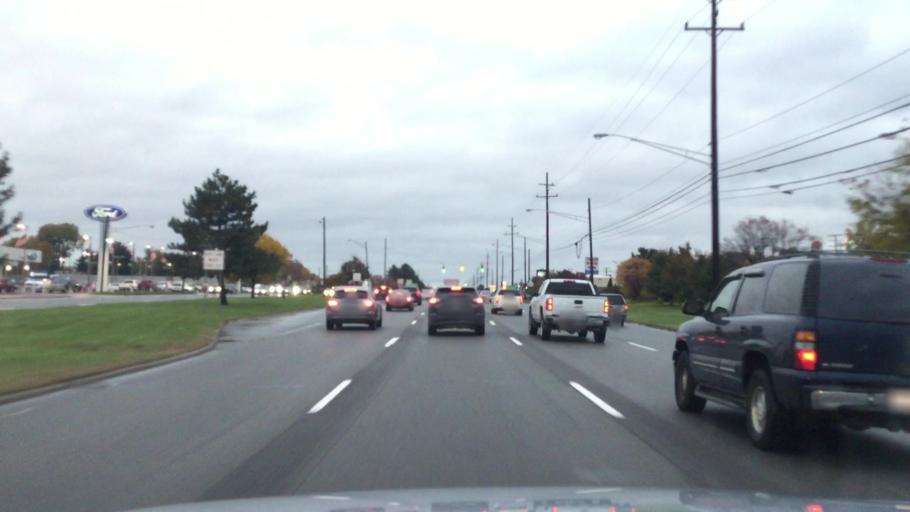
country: US
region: Michigan
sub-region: Wayne County
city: Redford
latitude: 42.3675
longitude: -83.2757
